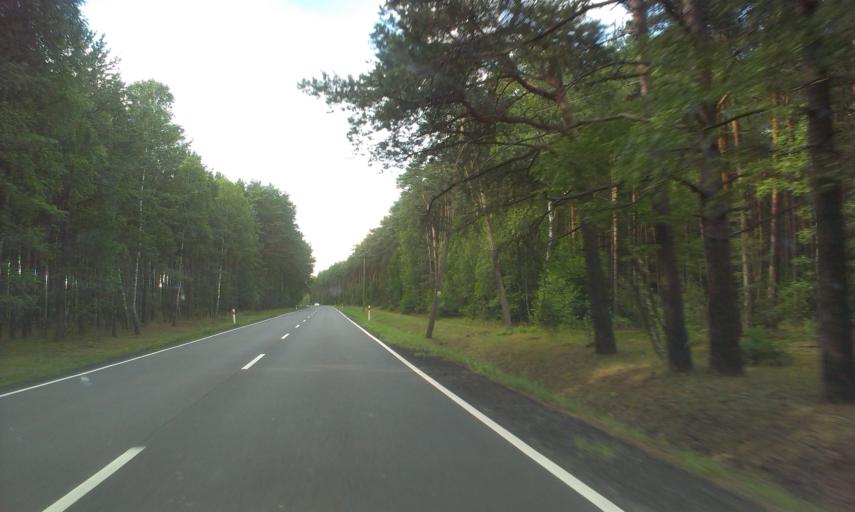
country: PL
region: Greater Poland Voivodeship
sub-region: Powiat zlotowski
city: Tarnowka
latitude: 53.3388
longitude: 16.7920
